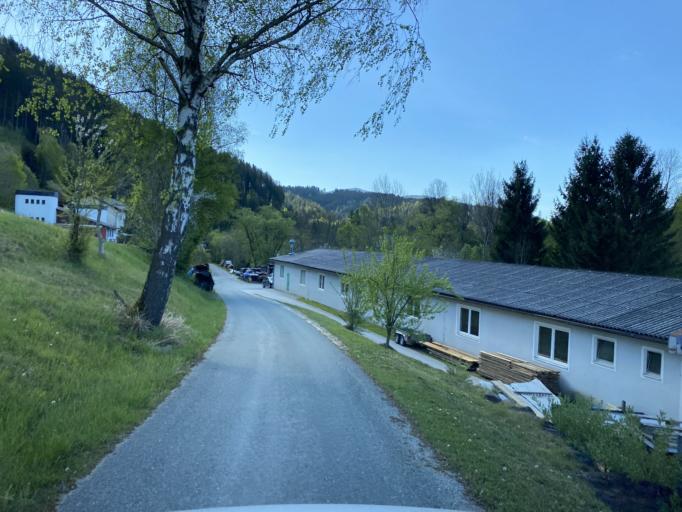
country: AT
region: Styria
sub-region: Politischer Bezirk Weiz
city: Birkfeld
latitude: 47.3591
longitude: 15.6991
